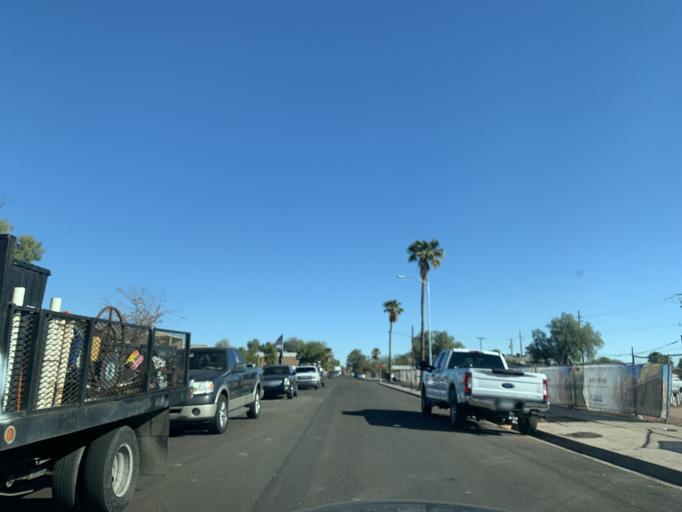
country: US
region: Arizona
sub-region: Maricopa County
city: Phoenix
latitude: 33.4504
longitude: -112.0511
